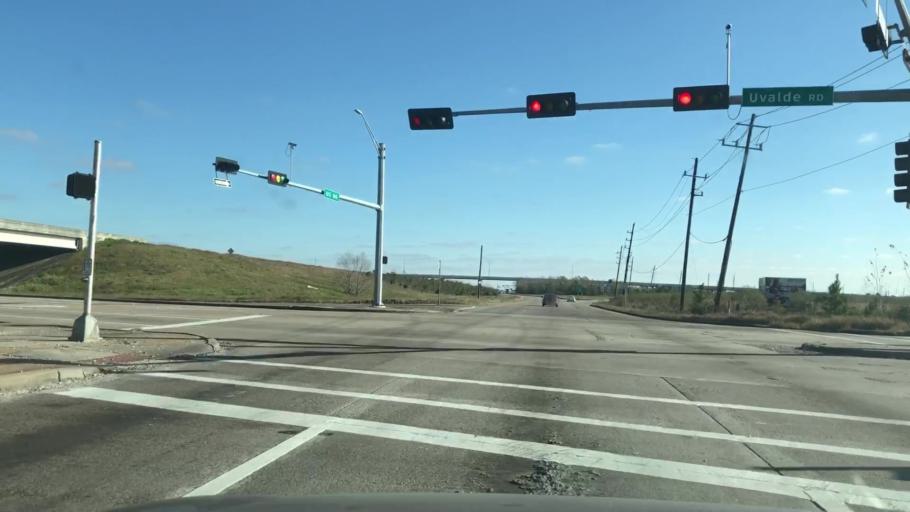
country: US
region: Texas
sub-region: Harris County
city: Cloverleaf
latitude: 29.8288
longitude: -95.1827
